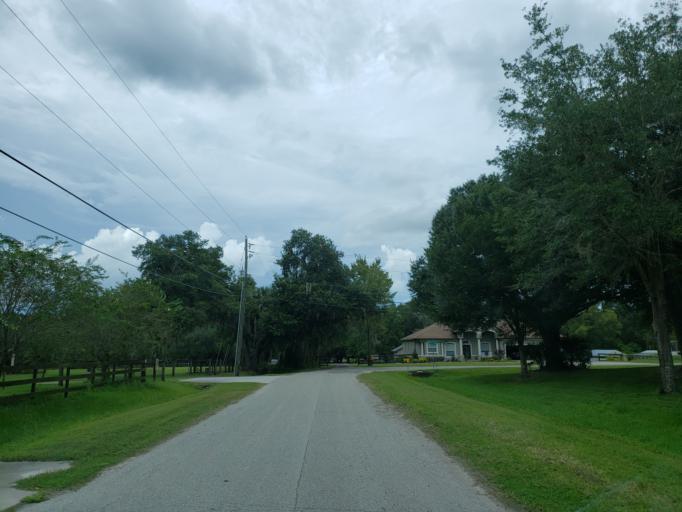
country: US
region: Florida
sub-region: Polk County
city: Willow Oak
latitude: 27.9616
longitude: -82.0513
